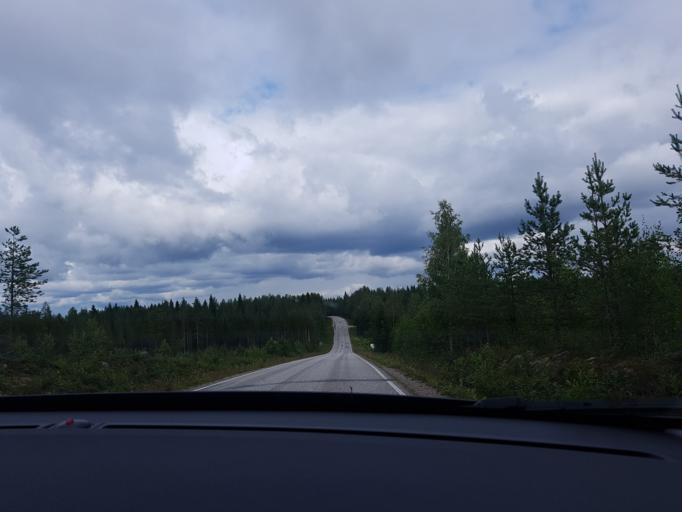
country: FI
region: Kainuu
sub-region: Kehys-Kainuu
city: Kuhmo
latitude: 64.2269
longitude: 29.4499
